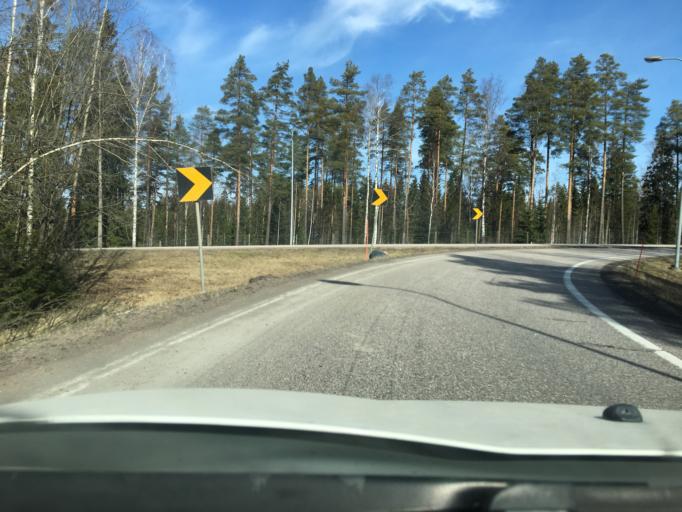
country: FI
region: Uusimaa
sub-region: Helsinki
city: Espoo
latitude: 60.2453
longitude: 24.5662
